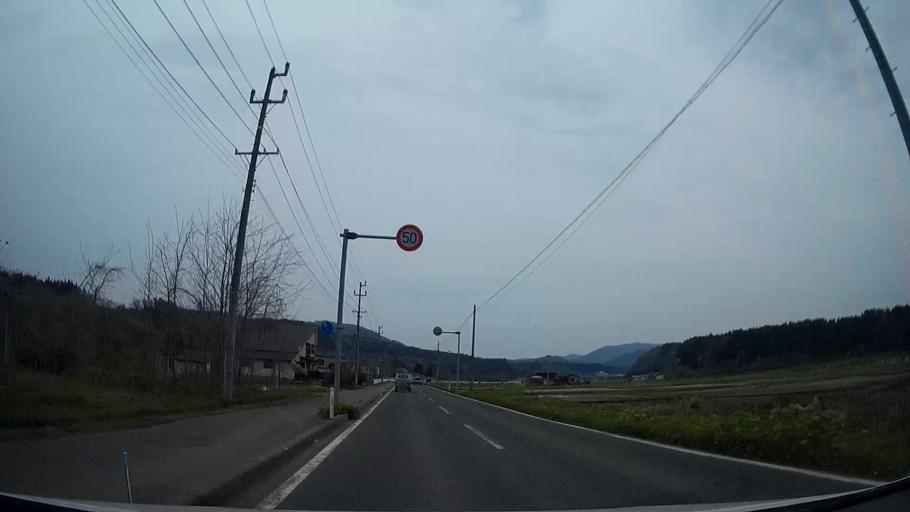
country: JP
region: Akita
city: Hanawa
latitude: 40.2838
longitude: 140.8031
